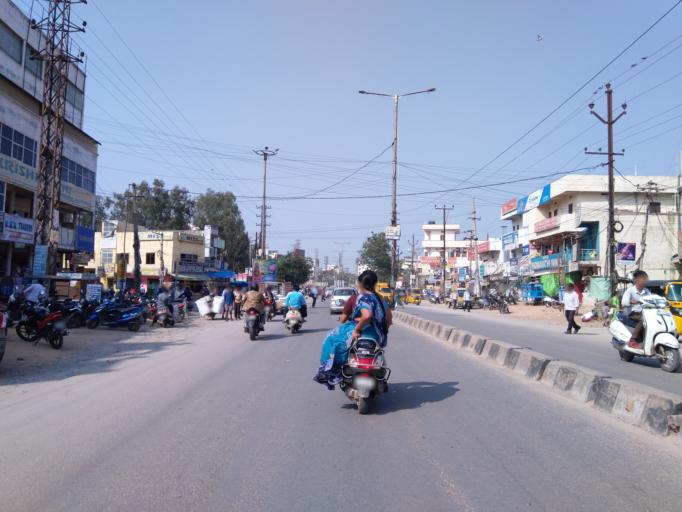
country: IN
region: Telangana
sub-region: Rangareddi
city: Quthbullapur
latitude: 17.5409
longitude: 78.4338
